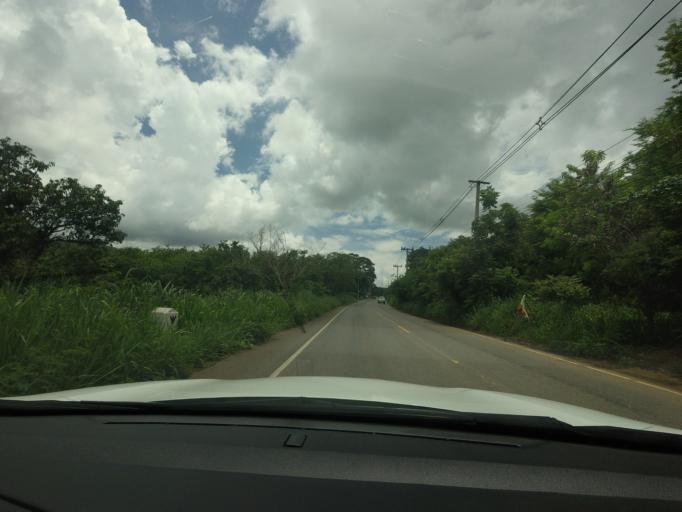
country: TH
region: Sara Buri
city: Muak Lek
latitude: 14.5451
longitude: 101.3311
